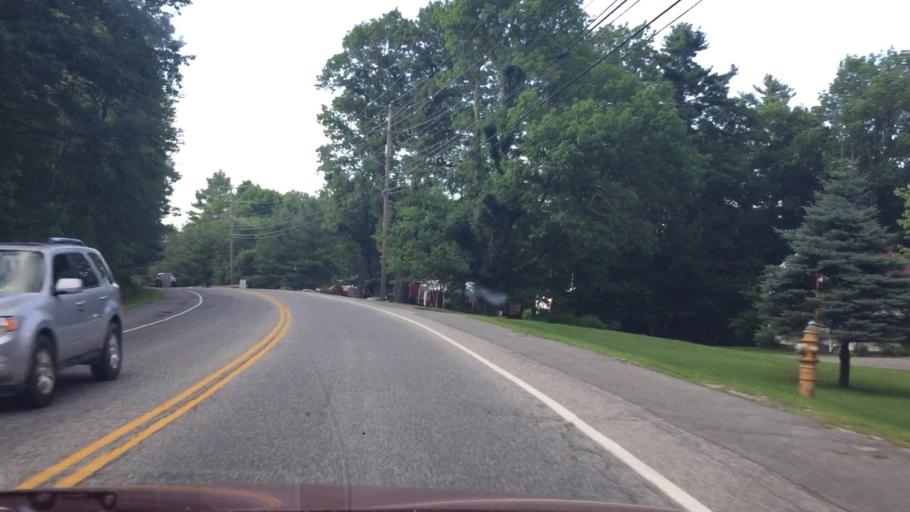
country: US
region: Maine
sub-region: Cumberland County
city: Westbrook
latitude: 43.6554
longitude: -70.3600
